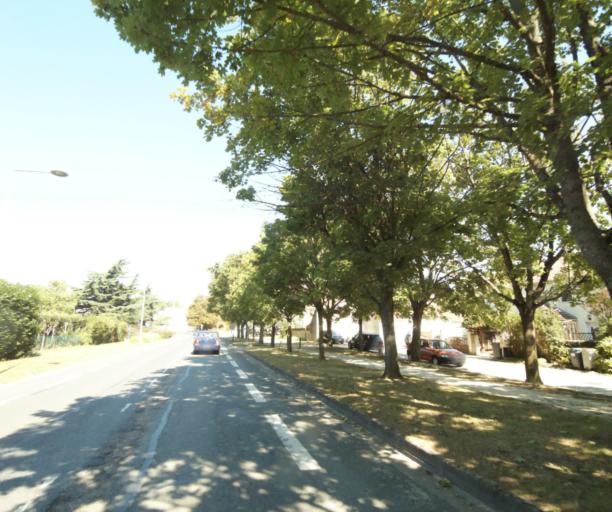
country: FR
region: Ile-de-France
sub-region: Departement de Seine-et-Marne
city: Moissy-Cramayel
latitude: 48.6227
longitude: 2.6002
